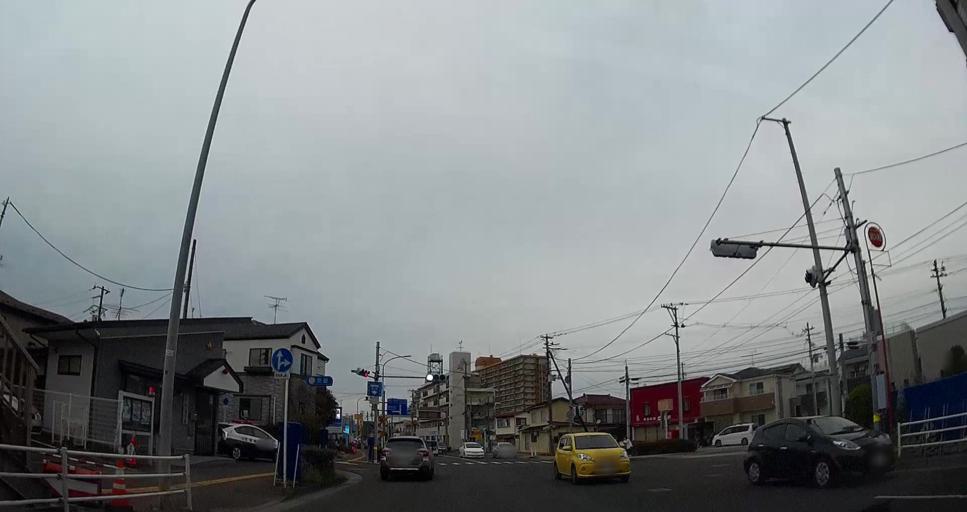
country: JP
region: Miyagi
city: Sendai
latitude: 38.2249
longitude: 140.8969
